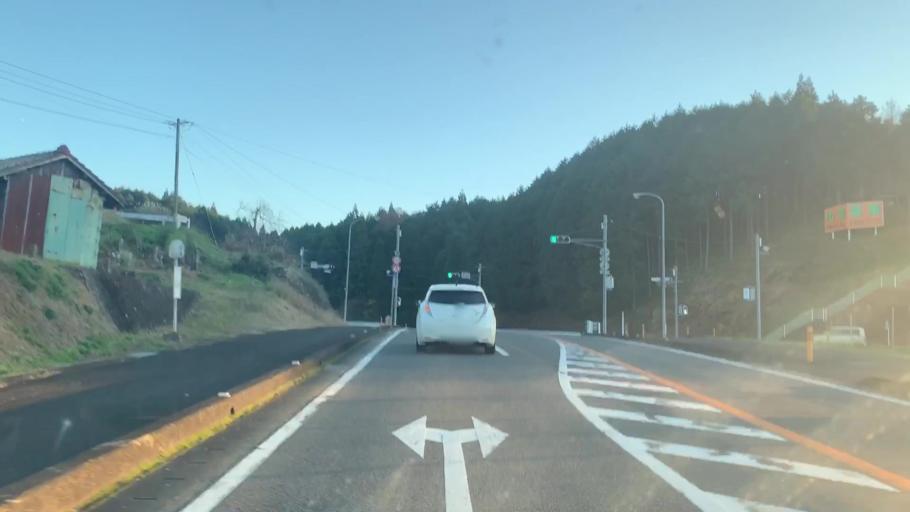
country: JP
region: Saga Prefecture
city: Imaricho-ko
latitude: 33.2643
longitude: 129.9658
